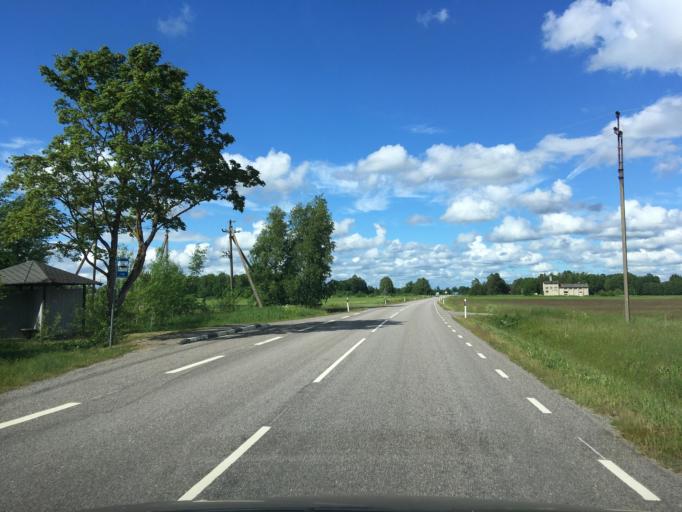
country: EE
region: Paernumaa
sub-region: Halinga vald
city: Parnu-Jaagupi
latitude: 58.6430
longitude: 24.5580
